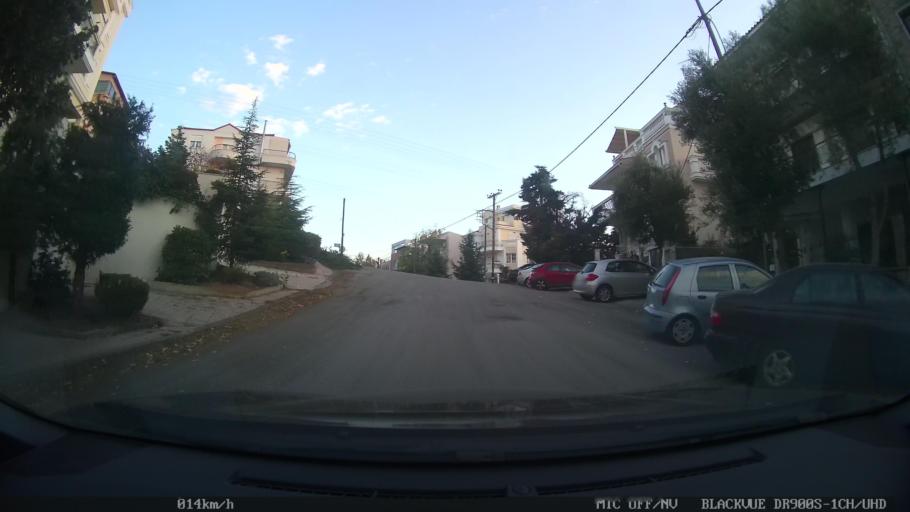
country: GR
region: Central Macedonia
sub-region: Nomos Thessalonikis
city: Pylaia
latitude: 40.6123
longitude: 22.9916
